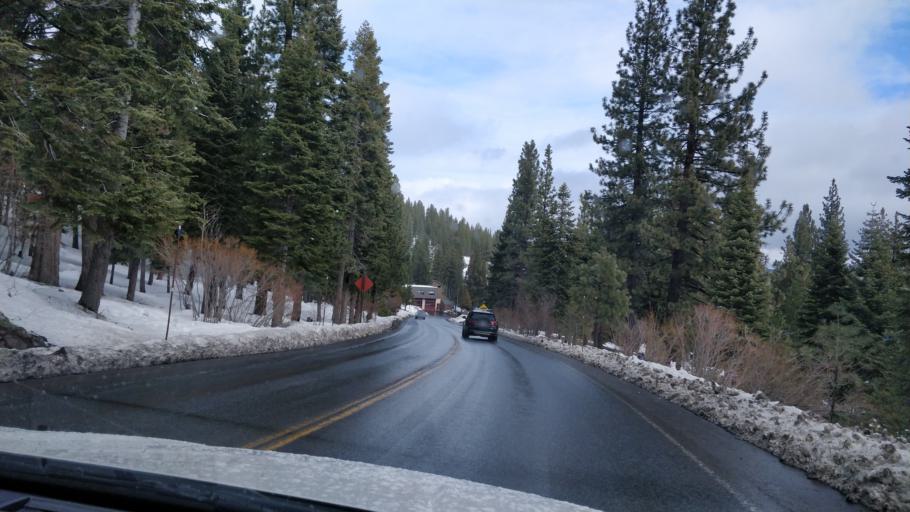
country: US
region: California
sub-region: Placer County
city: Tahoe Vista
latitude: 39.2786
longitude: -120.1199
